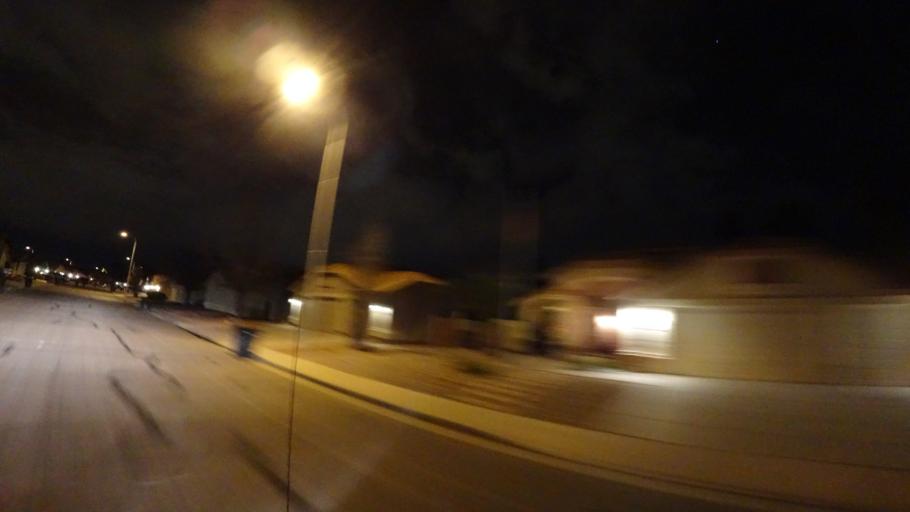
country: US
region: Arizona
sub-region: Maricopa County
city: Chandler
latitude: 33.2906
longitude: -111.8709
